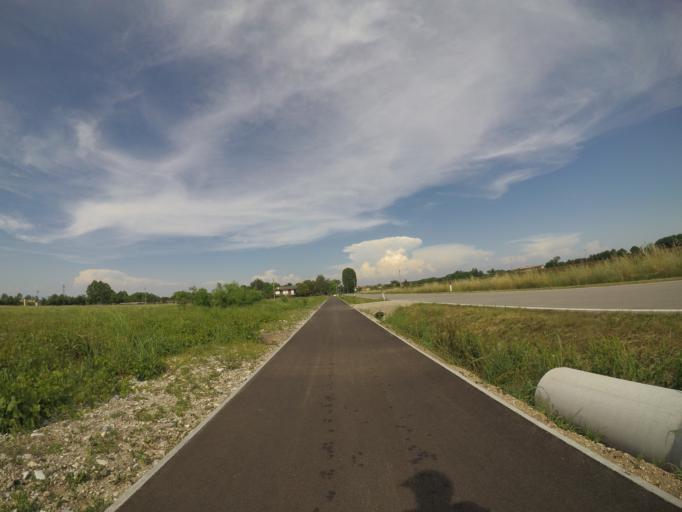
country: IT
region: Friuli Venezia Giulia
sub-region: Provincia di Udine
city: Codroipo
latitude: 45.9586
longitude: 12.9542
